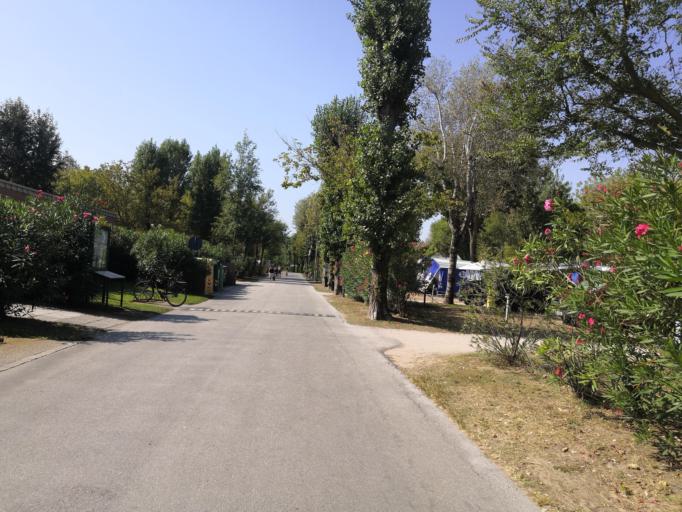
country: IT
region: Veneto
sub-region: Provincia di Venezia
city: Ca' Savio
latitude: 45.4355
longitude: 12.4409
